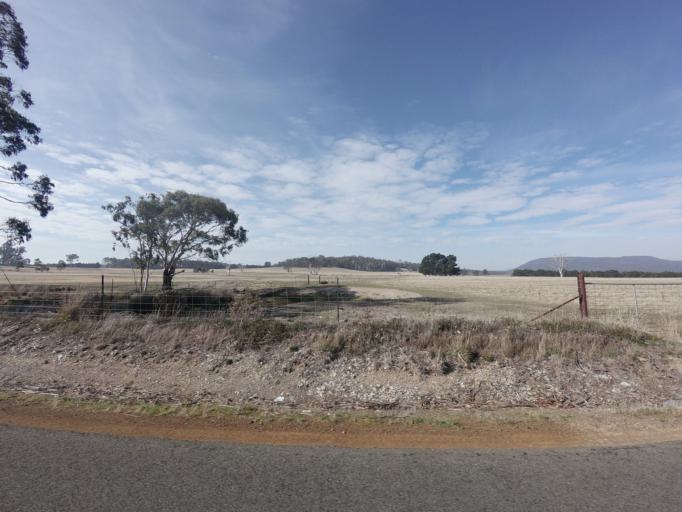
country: AU
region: Tasmania
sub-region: Sorell
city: Sorell
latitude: -42.4332
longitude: 147.4718
